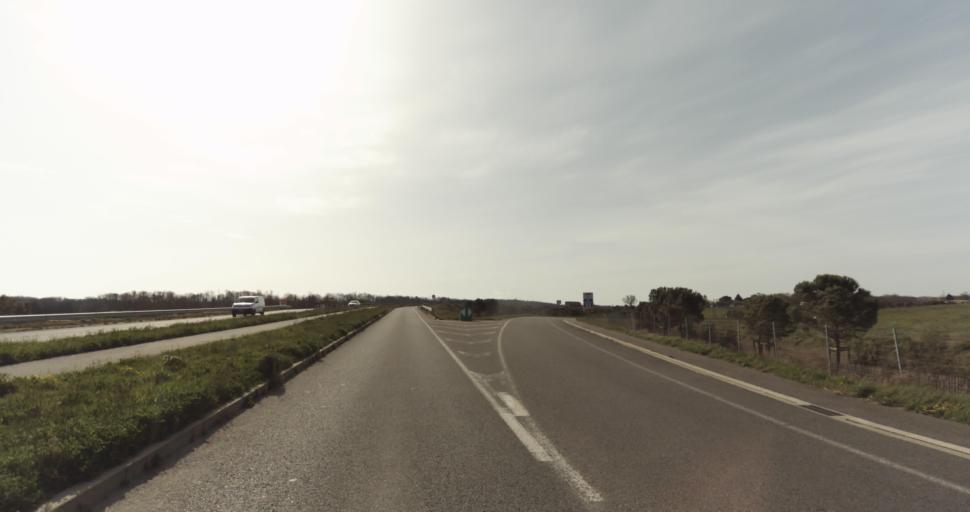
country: FR
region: Midi-Pyrenees
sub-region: Departement du Tarn
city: Saint-Sulpice-la-Pointe
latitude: 43.7559
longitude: 1.6594
